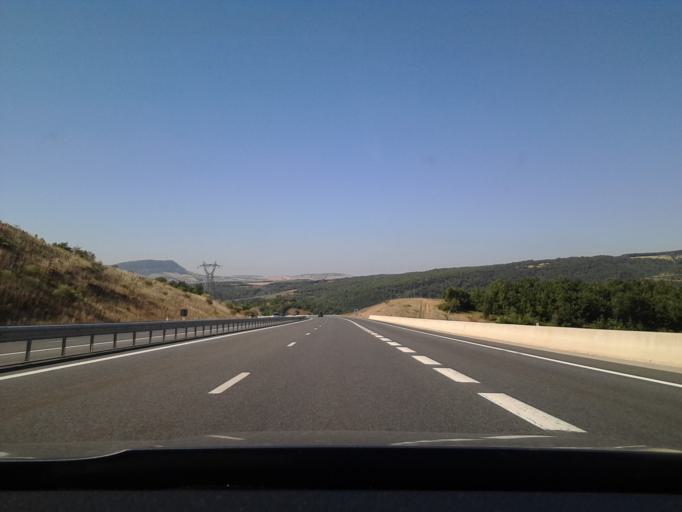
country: FR
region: Midi-Pyrenees
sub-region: Departement de l'Aveyron
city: Millau
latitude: 44.2119
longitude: 3.0696
